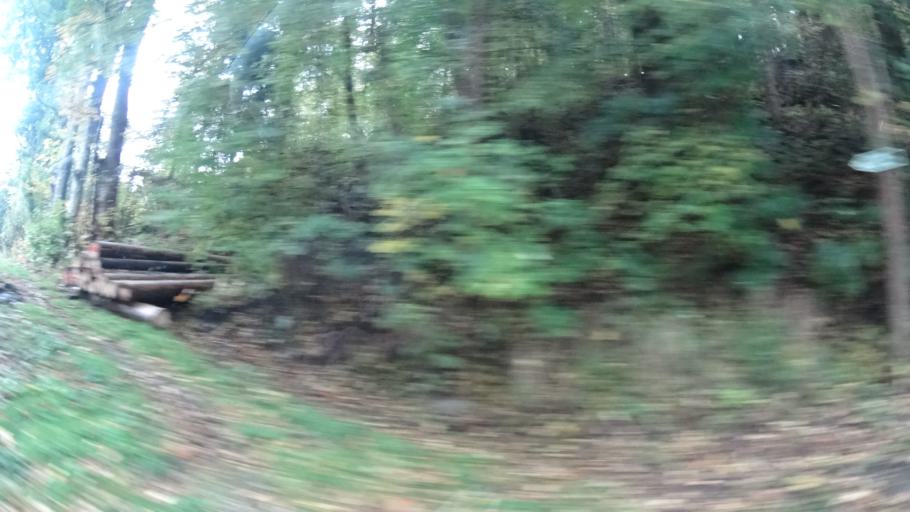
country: DE
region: Thuringia
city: Wurzbach
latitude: 50.4719
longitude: 11.5459
